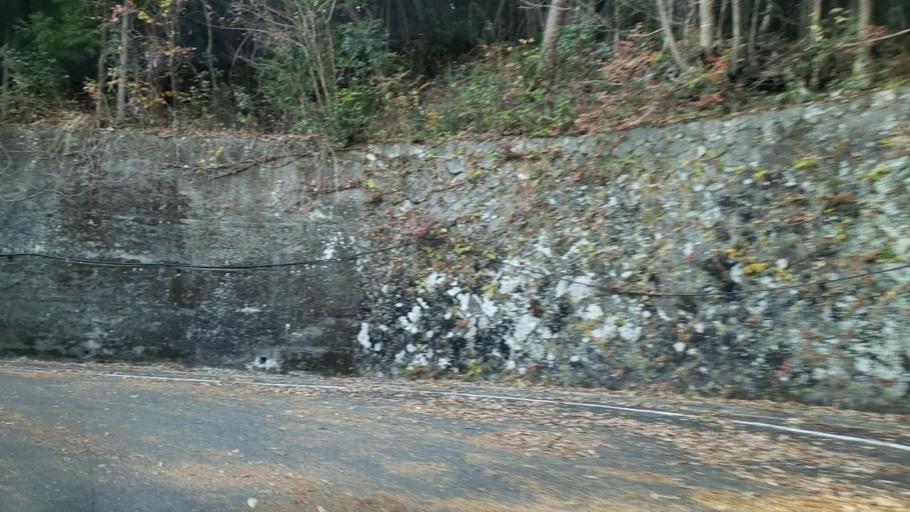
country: JP
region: Tokushima
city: Wakimachi
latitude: 34.1128
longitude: 134.0795
